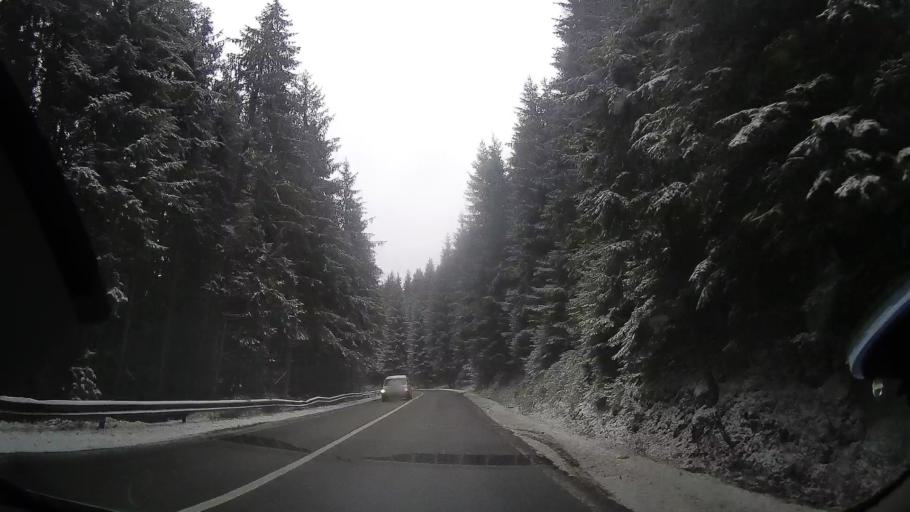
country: RO
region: Cluj
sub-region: Comuna Belis
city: Belis
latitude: 46.6726
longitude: 23.0450
